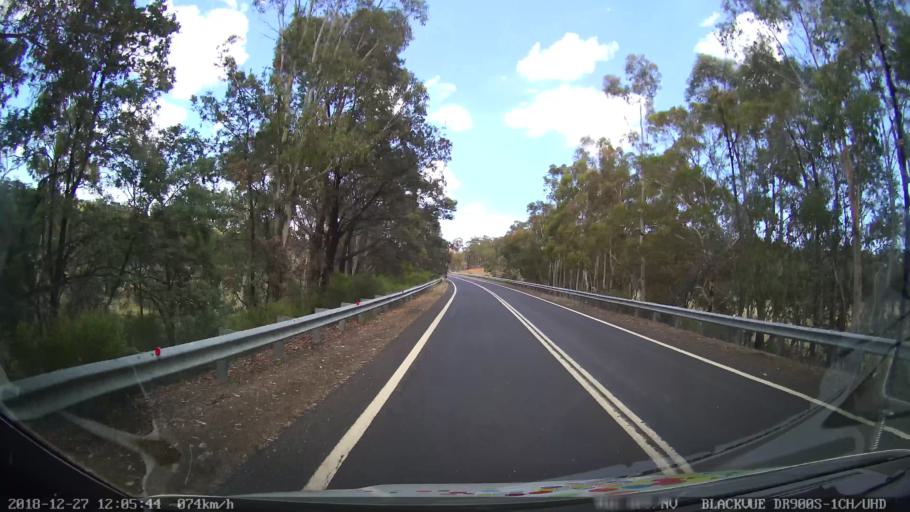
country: AU
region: New South Wales
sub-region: Blayney
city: Blayney
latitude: -33.8036
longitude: 149.3354
